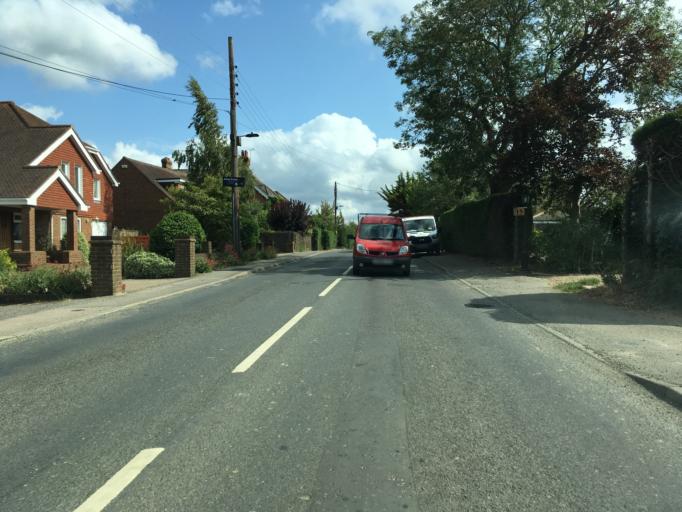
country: GB
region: England
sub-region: Kent
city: Headcorn
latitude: 51.1723
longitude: 0.6172
